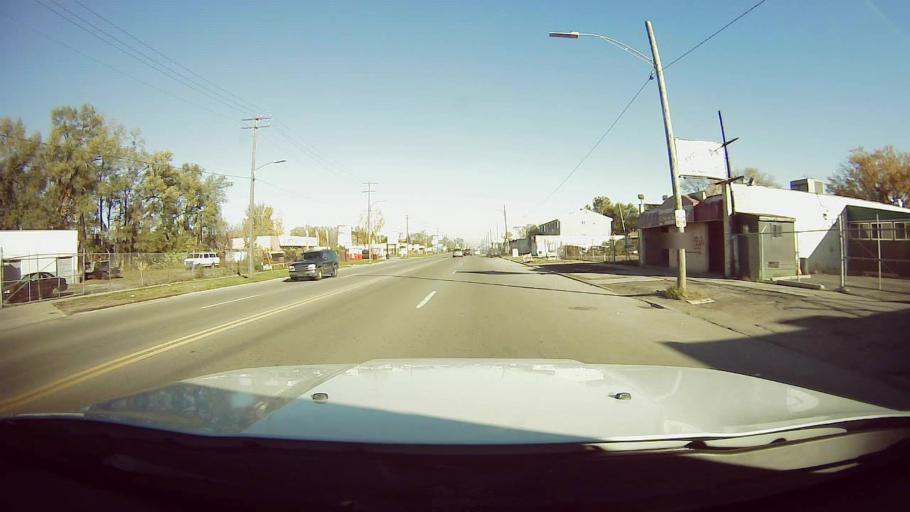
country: US
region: Michigan
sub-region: Wayne County
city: Dearborn
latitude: 42.3610
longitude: -83.1970
